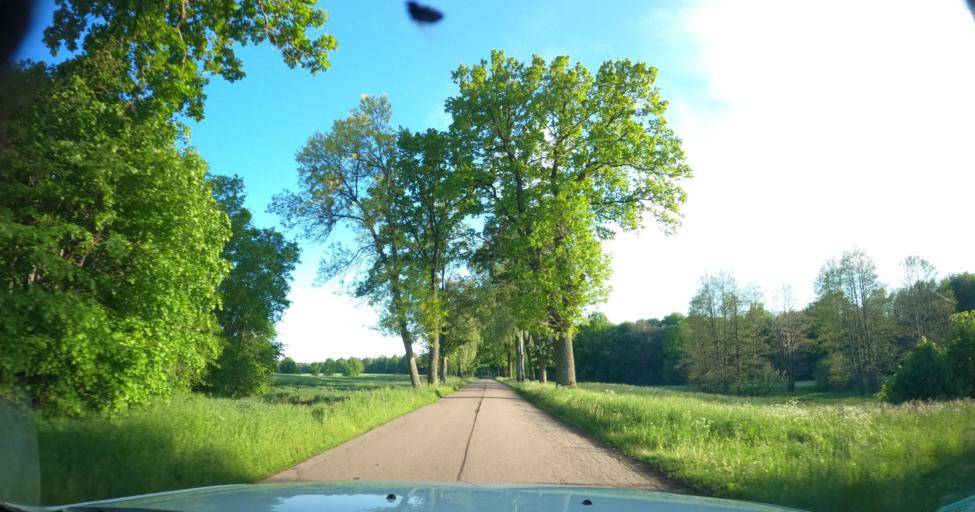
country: PL
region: Warmian-Masurian Voivodeship
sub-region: Powiat braniewski
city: Pieniezno
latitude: 54.2238
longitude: 20.0347
